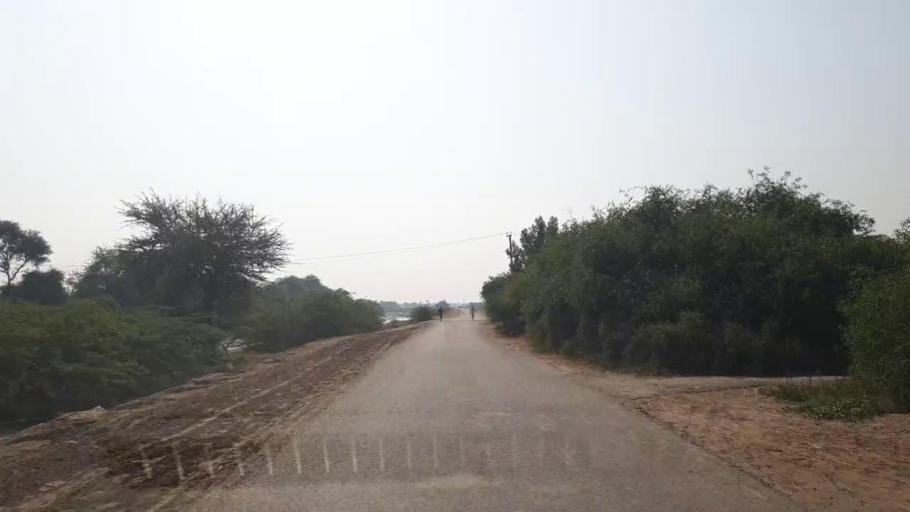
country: PK
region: Sindh
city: Matli
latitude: 24.9667
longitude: 68.5993
